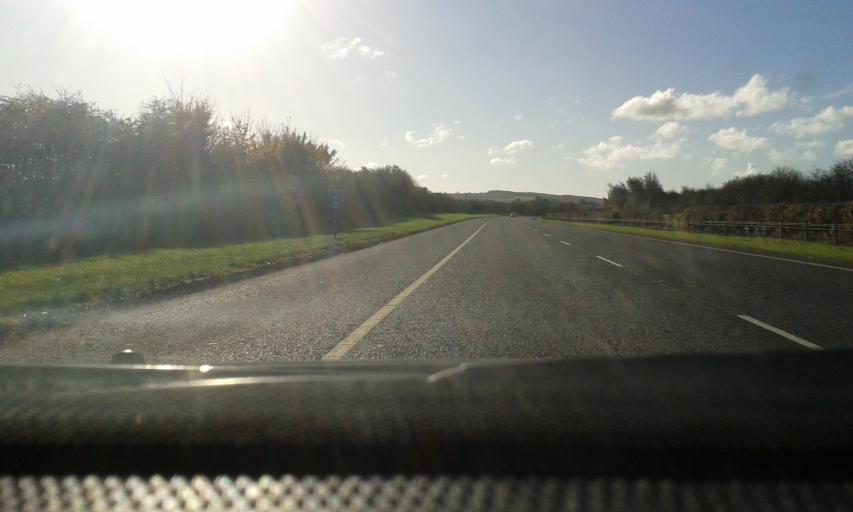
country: IE
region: Leinster
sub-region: Laois
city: Portlaoise
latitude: 53.0414
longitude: -7.2436
